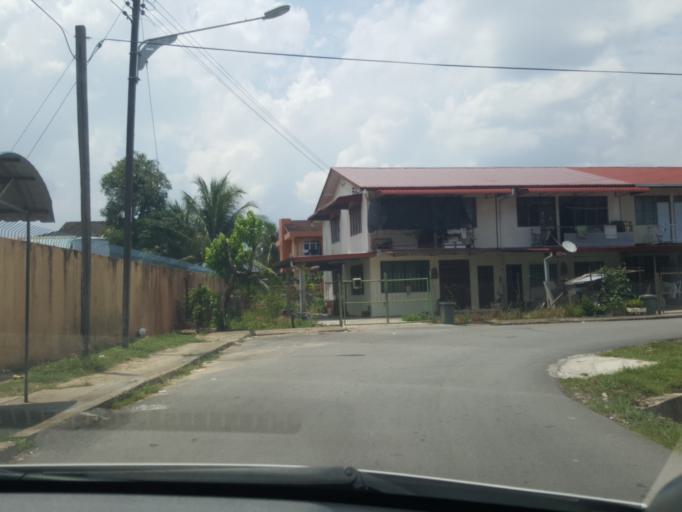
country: MY
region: Sarawak
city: Sarikei
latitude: 2.1255
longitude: 111.5211
